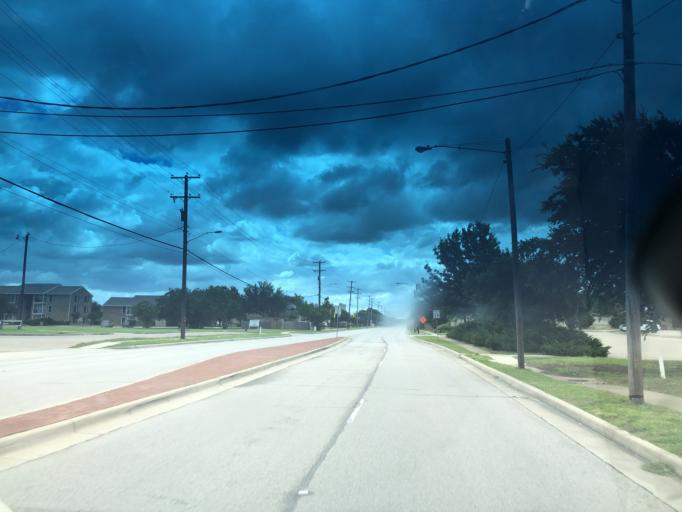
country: US
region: Texas
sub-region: Dallas County
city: Grand Prairie
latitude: 32.6980
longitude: -97.0152
